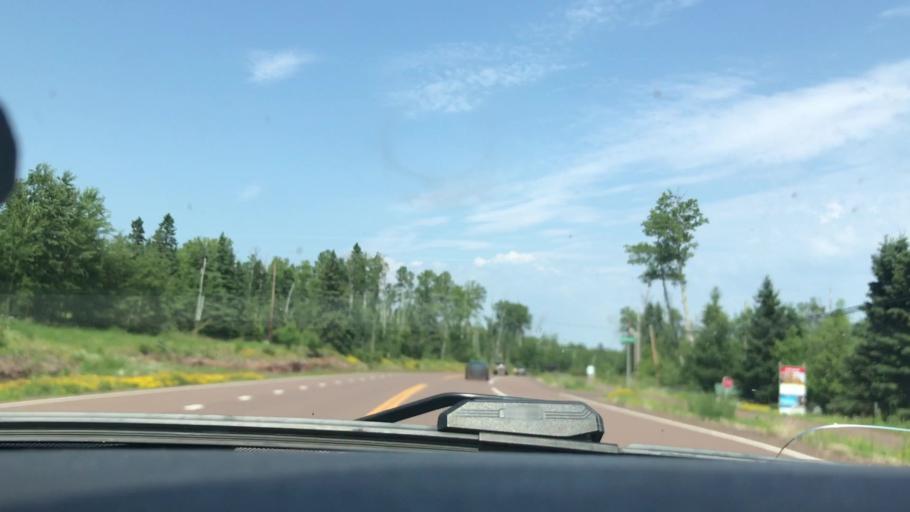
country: US
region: Minnesota
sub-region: Cook County
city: Grand Marais
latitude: 47.6058
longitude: -90.7791
